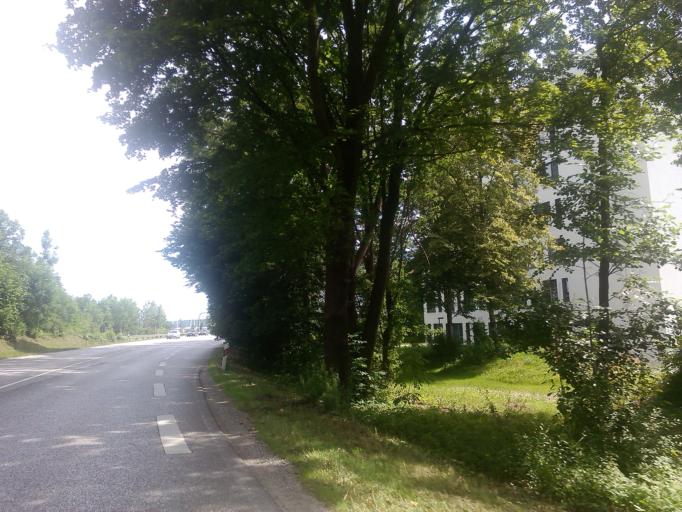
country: DE
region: Bavaria
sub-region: Upper Bavaria
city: Gilching
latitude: 48.0920
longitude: 11.2807
